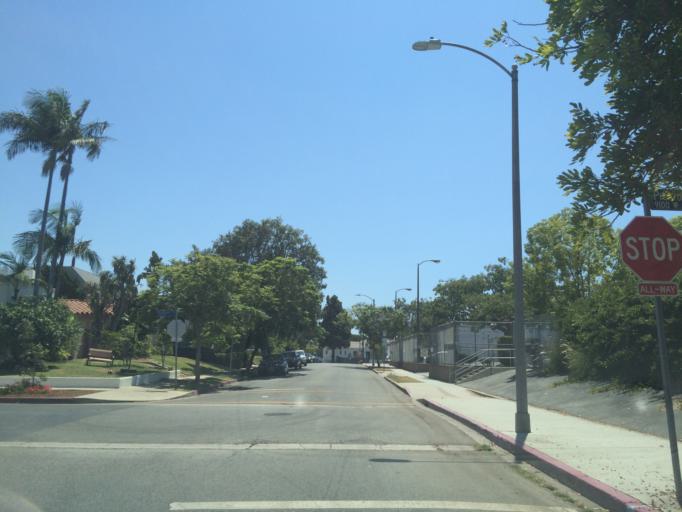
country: US
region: California
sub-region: Los Angeles County
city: Beverly Hills
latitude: 34.0510
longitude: -118.3896
